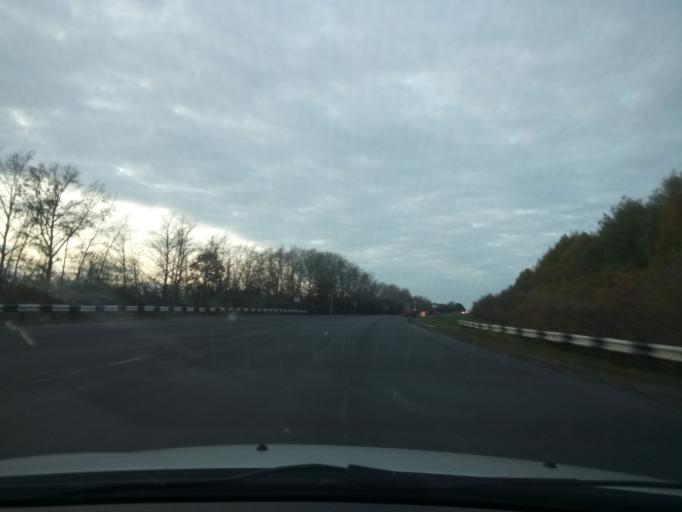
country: RU
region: Nizjnij Novgorod
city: Bol'shoye Murashkino
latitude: 55.8024
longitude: 44.7644
